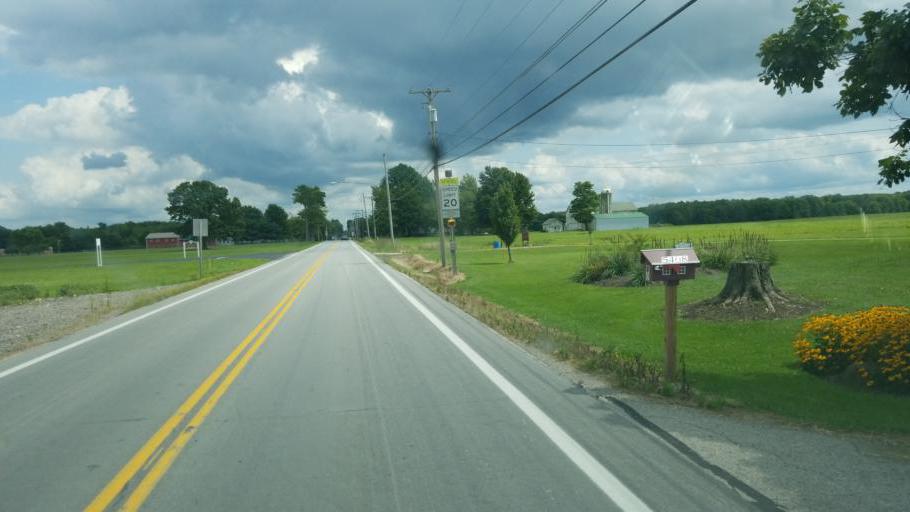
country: US
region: Ohio
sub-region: Ashtabula County
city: Andover
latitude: 41.6071
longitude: -80.5905
